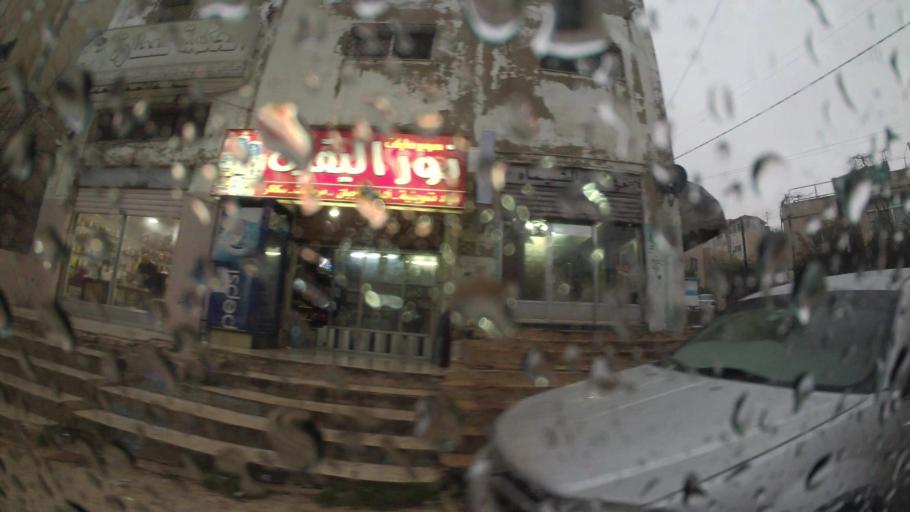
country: JO
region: Amman
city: Al Jubayhah
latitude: 32.0258
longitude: 35.8448
